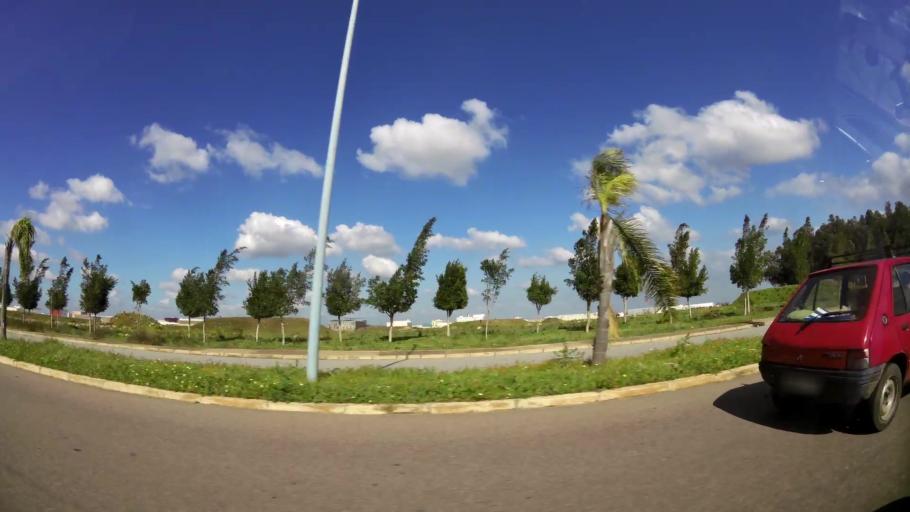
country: MA
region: Grand Casablanca
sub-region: Mediouna
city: Mediouna
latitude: 33.3972
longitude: -7.5542
